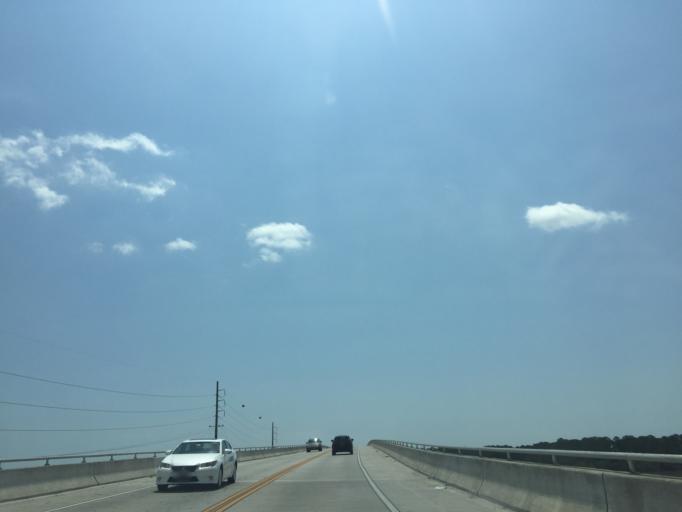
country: US
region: Georgia
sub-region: Chatham County
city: Skidaway Island
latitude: 31.9490
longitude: -81.0678
